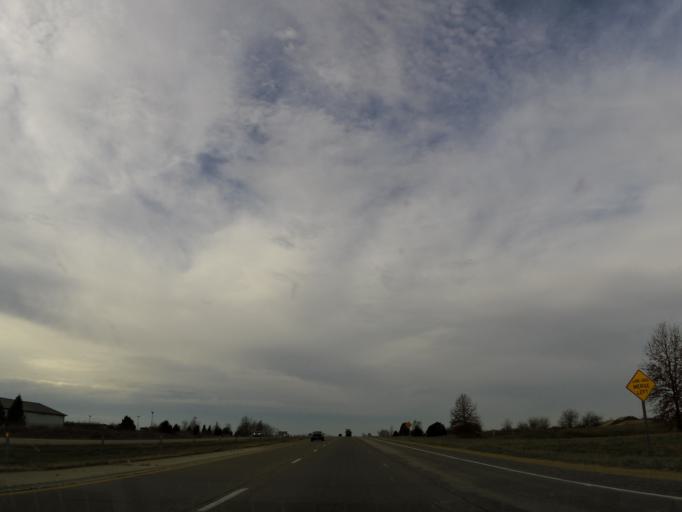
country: US
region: Iowa
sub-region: Scott County
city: Eldridge
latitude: 41.5973
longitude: -90.5765
